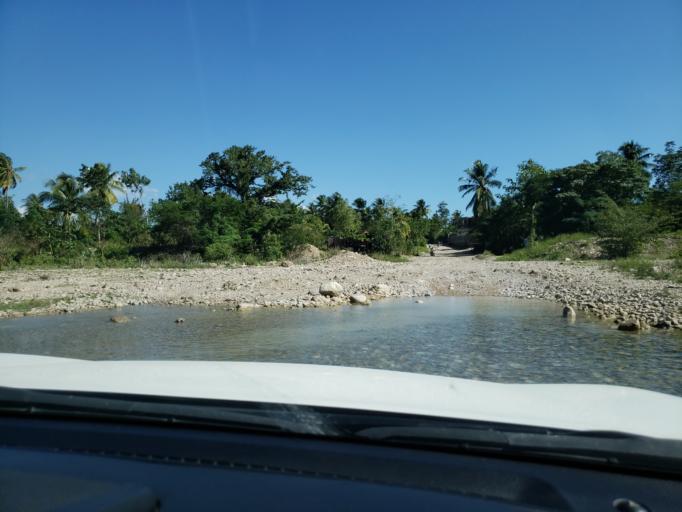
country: HT
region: Sud
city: Aquin
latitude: 18.3775
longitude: -73.4101
